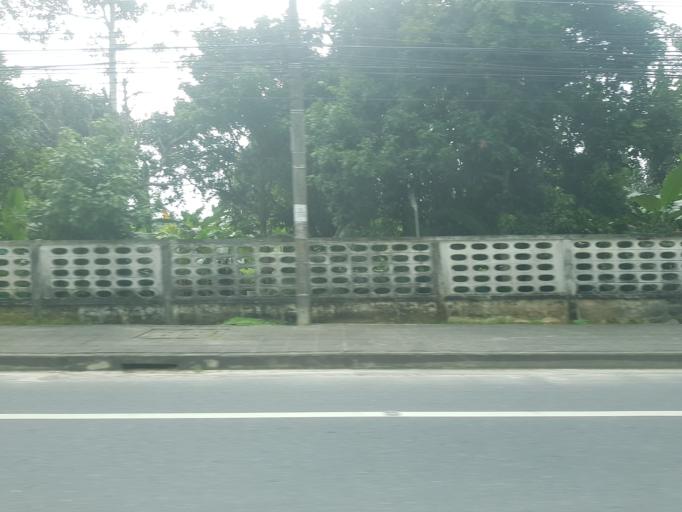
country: TH
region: Surat Thani
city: Ko Samui
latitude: 9.4714
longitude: 99.9610
